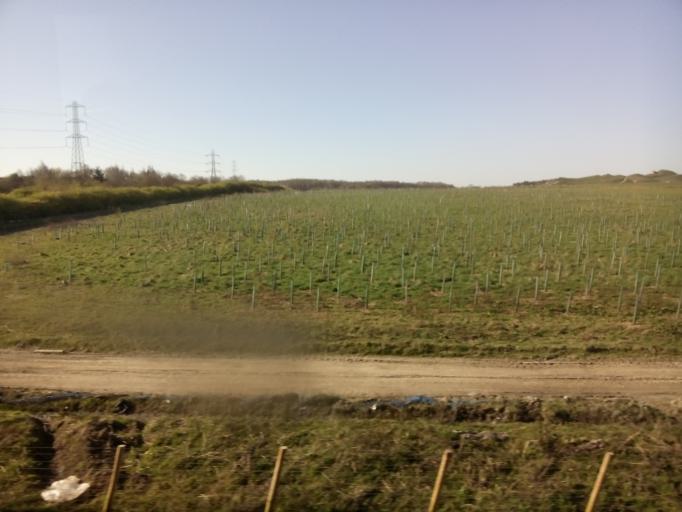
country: GB
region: England
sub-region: Northumberland
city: Cramlington
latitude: 55.0958
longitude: -1.6182
